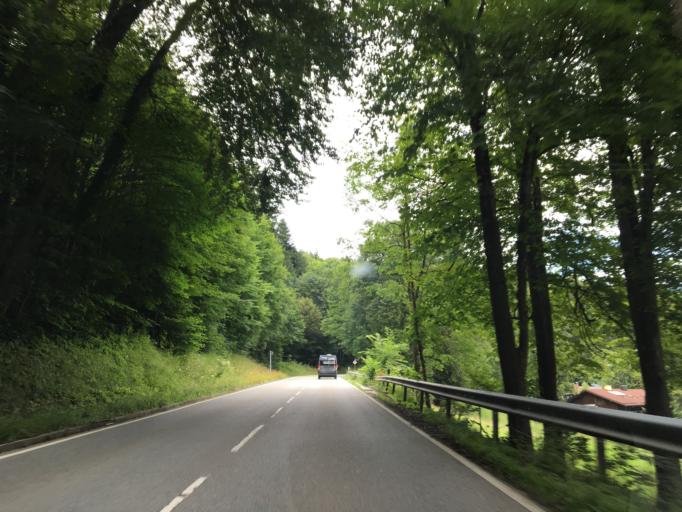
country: DE
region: Bavaria
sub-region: Upper Bavaria
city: Miesbach
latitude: 47.7825
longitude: 11.8743
